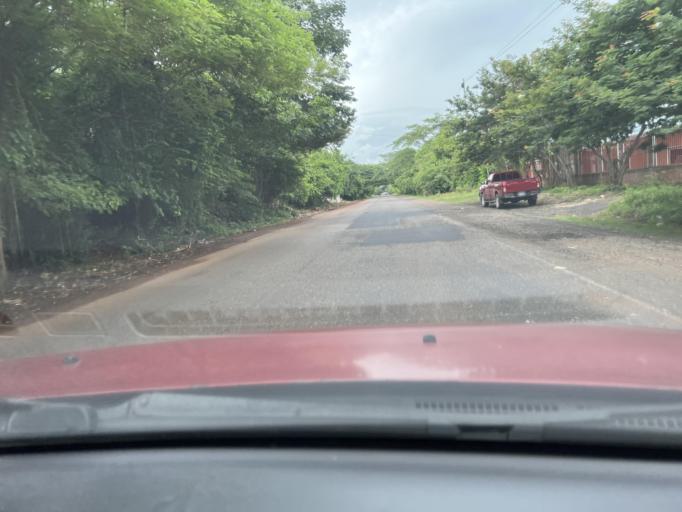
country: SV
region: La Union
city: San Alejo
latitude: 13.4064
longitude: -87.8926
